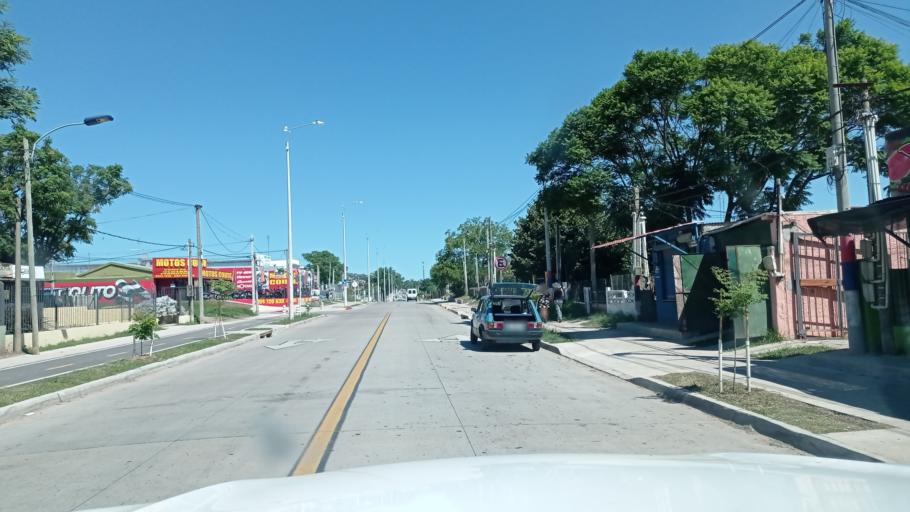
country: UY
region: Montevideo
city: Montevideo
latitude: -34.8673
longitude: -56.2681
